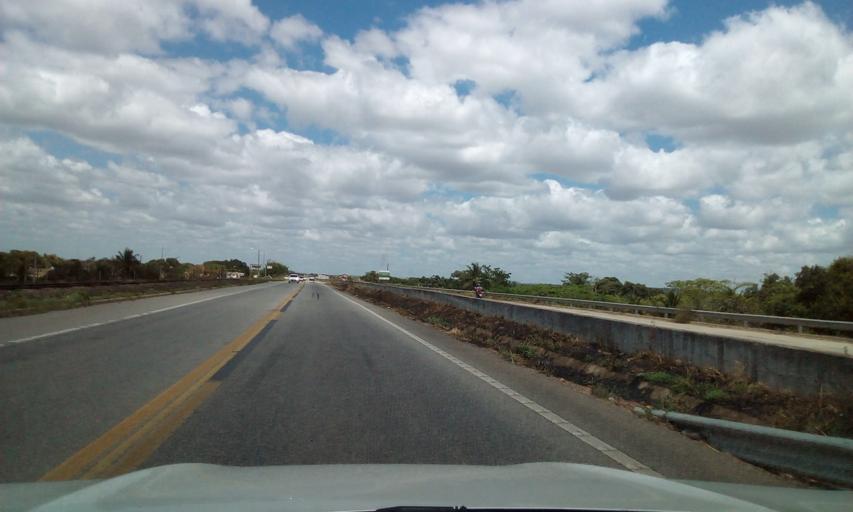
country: BR
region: Sergipe
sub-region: Propria
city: Propria
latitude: -10.2005
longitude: -36.8199
